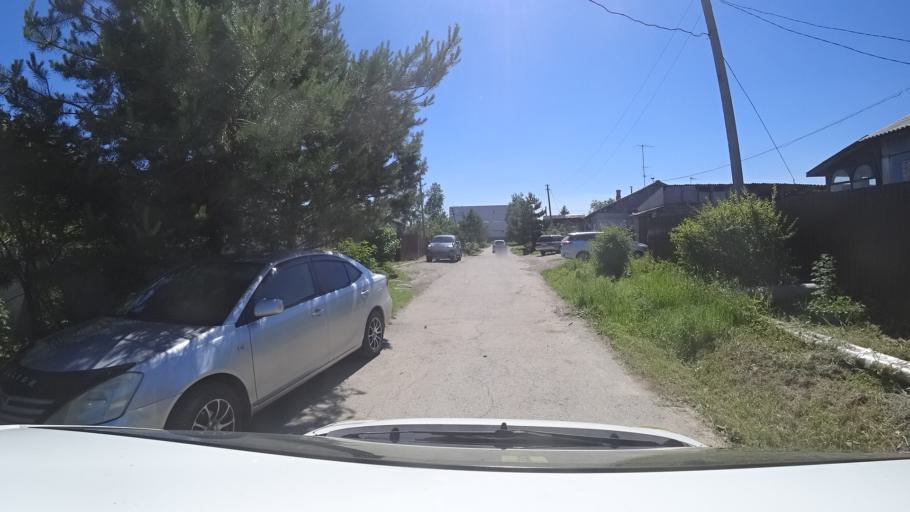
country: RU
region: Khabarovsk Krai
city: Topolevo
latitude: 48.5023
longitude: 135.1759
